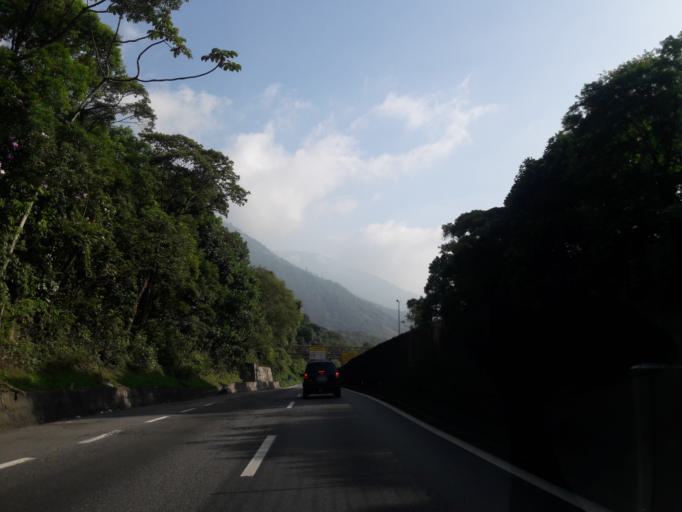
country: BR
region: Sao Paulo
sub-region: Cubatao
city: Cubatao
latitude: -23.8859
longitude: -46.4618
